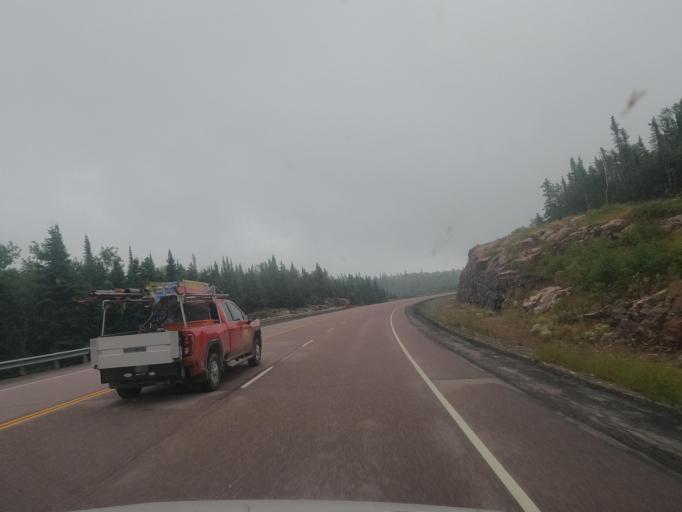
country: CA
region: Ontario
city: Greenstone
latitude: 48.9086
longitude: -87.6581
